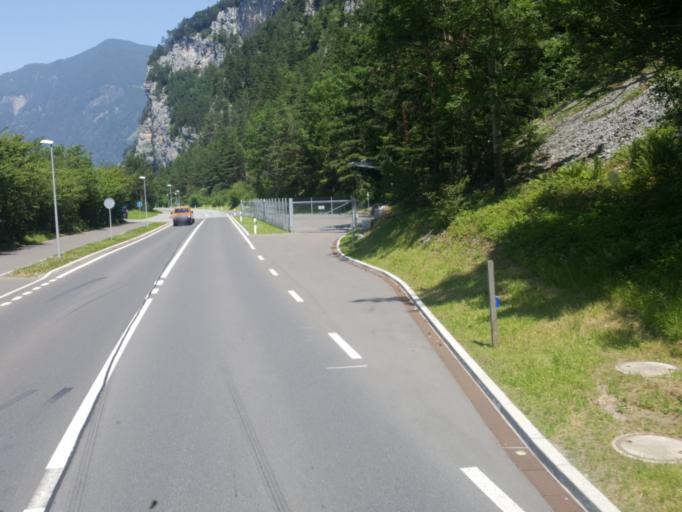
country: CH
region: Uri
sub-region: Uri
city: Attinghausen
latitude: 46.8437
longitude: 8.6449
